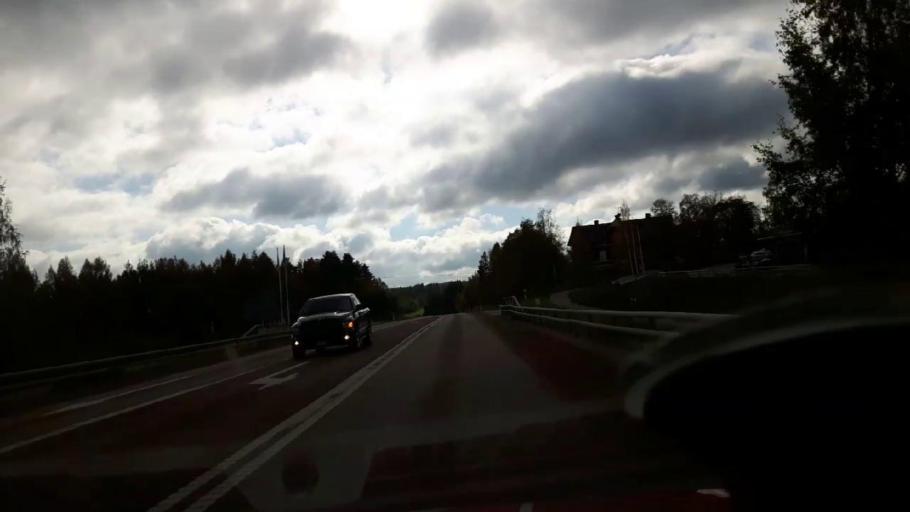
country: SE
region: Gaevleborg
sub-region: Ljusdals Kommun
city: Jaervsoe
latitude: 61.6723
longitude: 16.1454
